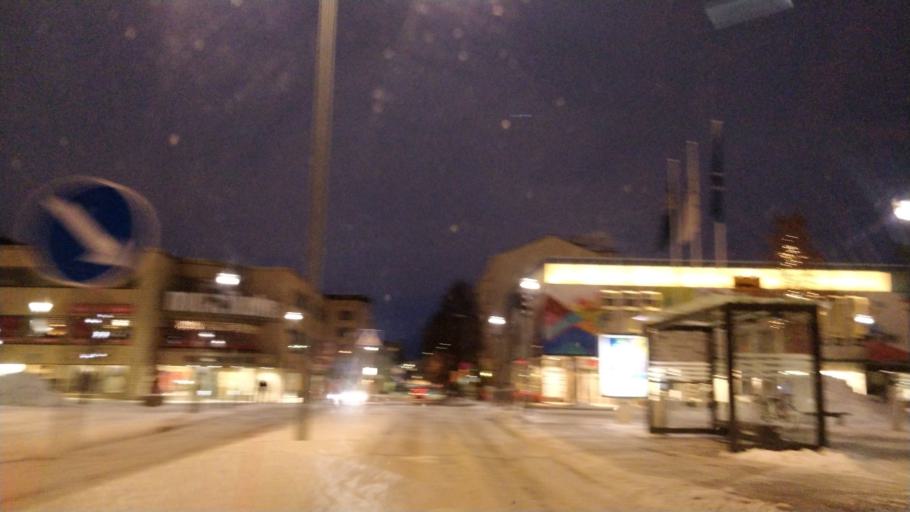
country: FI
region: Lapland
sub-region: Kemi-Tornio
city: Kemi
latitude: 65.7381
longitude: 24.5651
